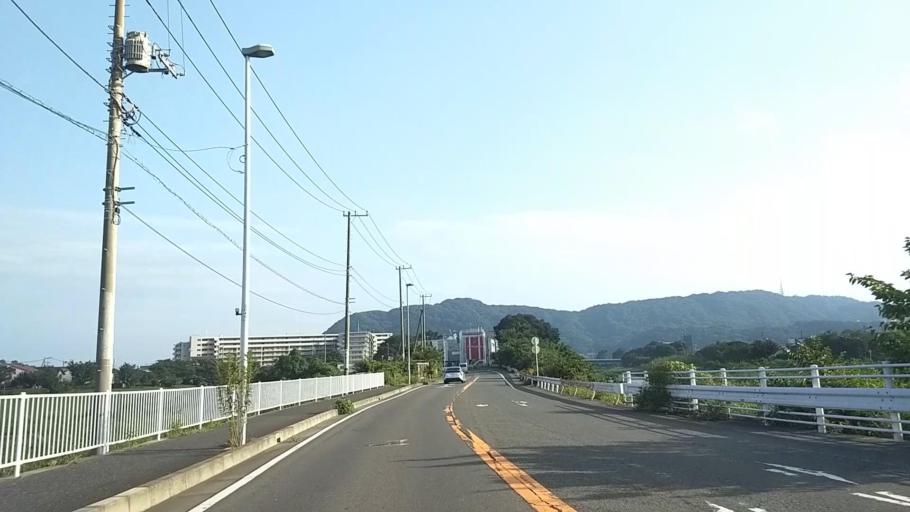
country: JP
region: Kanagawa
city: Hiratsuka
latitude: 35.3393
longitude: 139.3222
